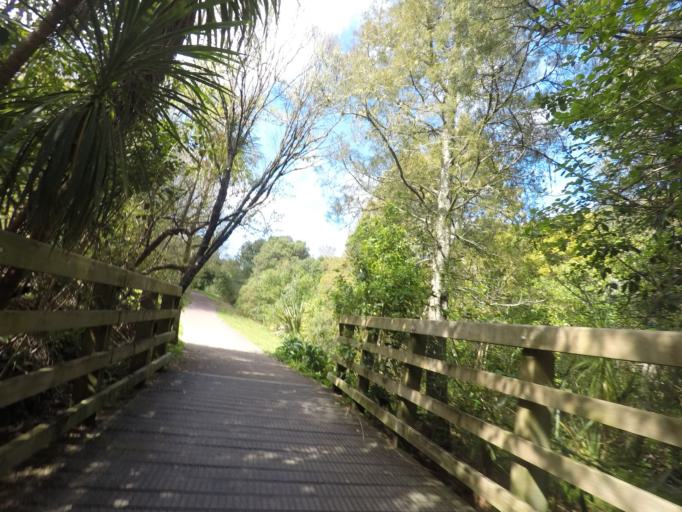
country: NZ
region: Auckland
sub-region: Auckland
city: Auckland
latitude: -36.8530
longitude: 174.7315
